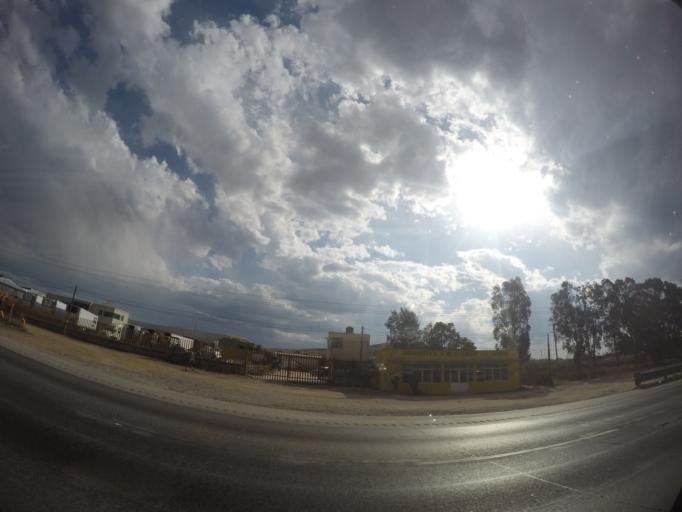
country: MX
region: Hidalgo
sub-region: Tepeji del Rio de Ocampo
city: Santiago Tlautla
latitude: 19.9831
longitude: -99.4385
